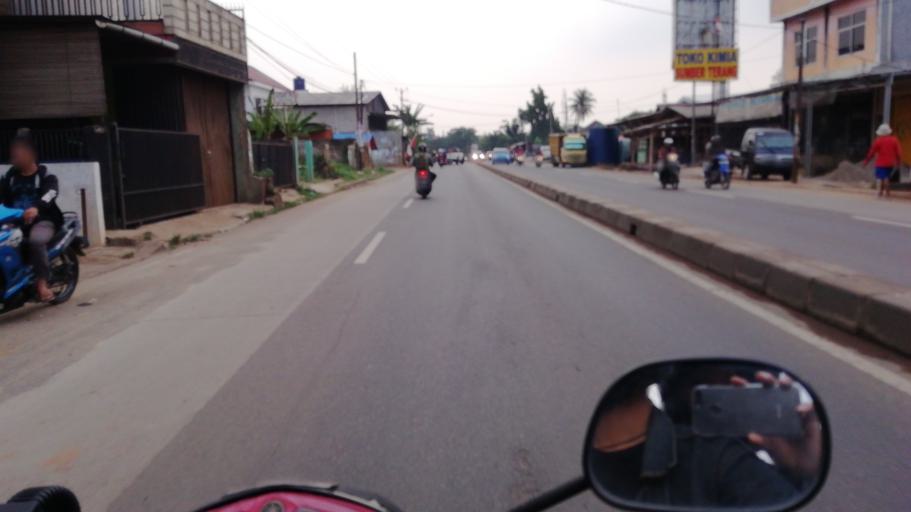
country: ID
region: West Java
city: Parung
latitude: -6.4636
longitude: 106.7297
